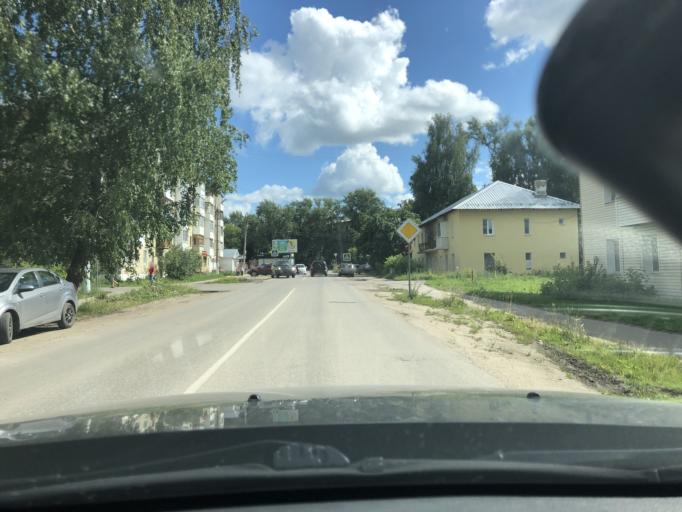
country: RU
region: Tula
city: Kimovsk
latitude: 53.9749
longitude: 38.5306
